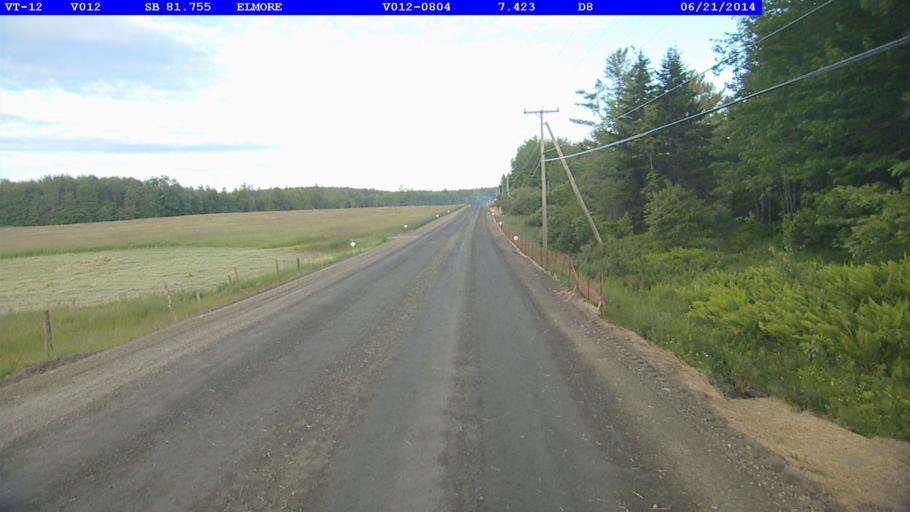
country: US
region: Vermont
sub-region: Lamoille County
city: Morrisville
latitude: 44.5479
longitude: -72.5326
